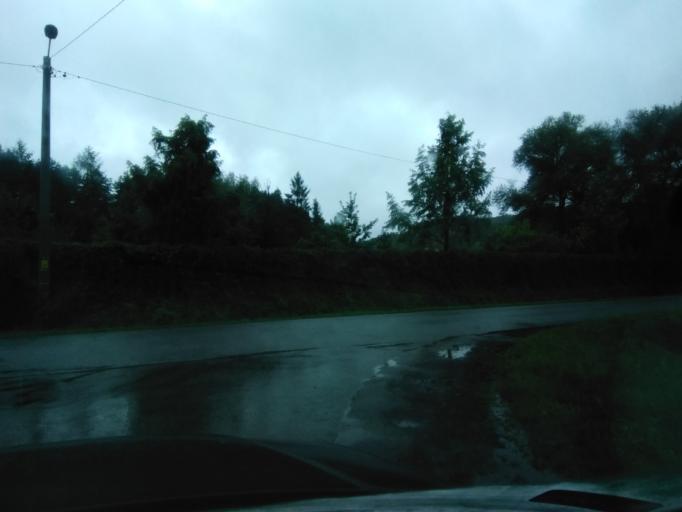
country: PL
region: Subcarpathian Voivodeship
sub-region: Powiat ropczycko-sedziszowski
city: Niedzwiada
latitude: 50.0310
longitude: 21.5475
